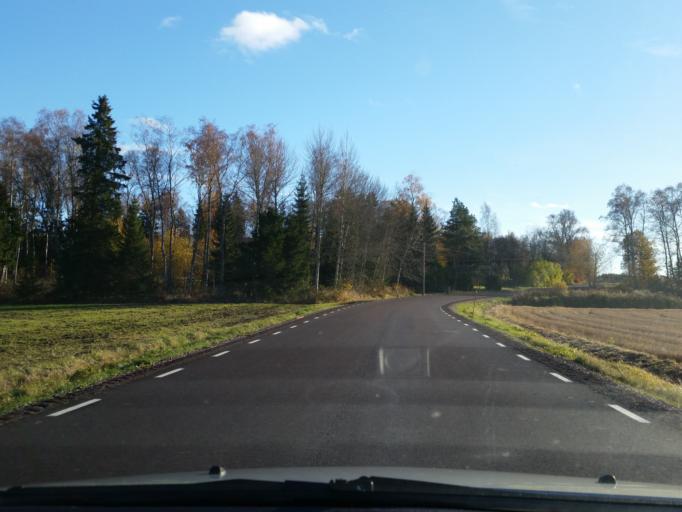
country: AX
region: Alands landsbygd
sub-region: Jomala
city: Jomala
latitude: 60.1913
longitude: 19.9602
